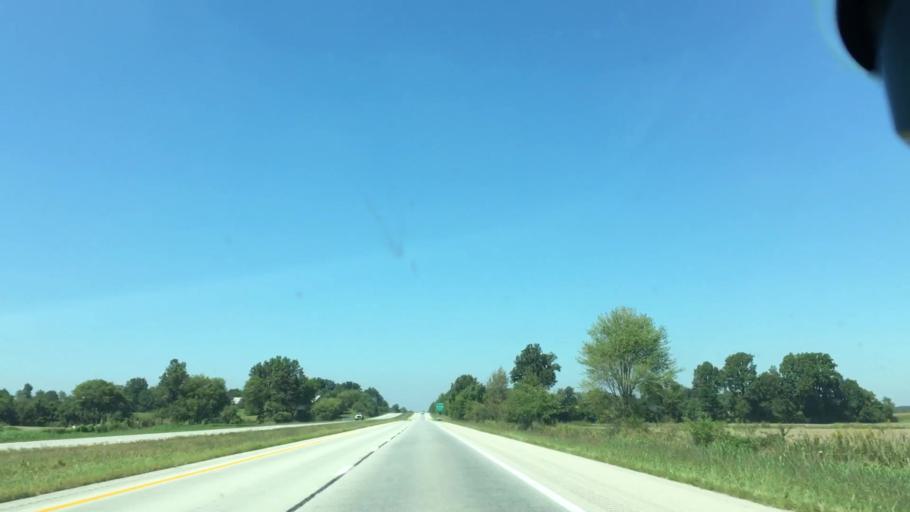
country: US
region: Kentucky
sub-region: Henderson County
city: Henderson
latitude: 37.7684
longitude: -87.5347
